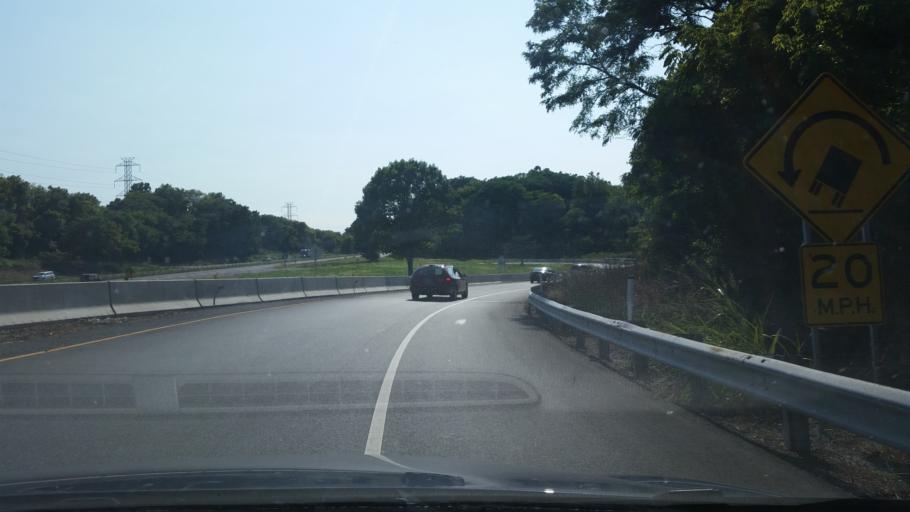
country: US
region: Pennsylvania
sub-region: Berks County
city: Temple
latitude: 40.4120
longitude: -75.9391
